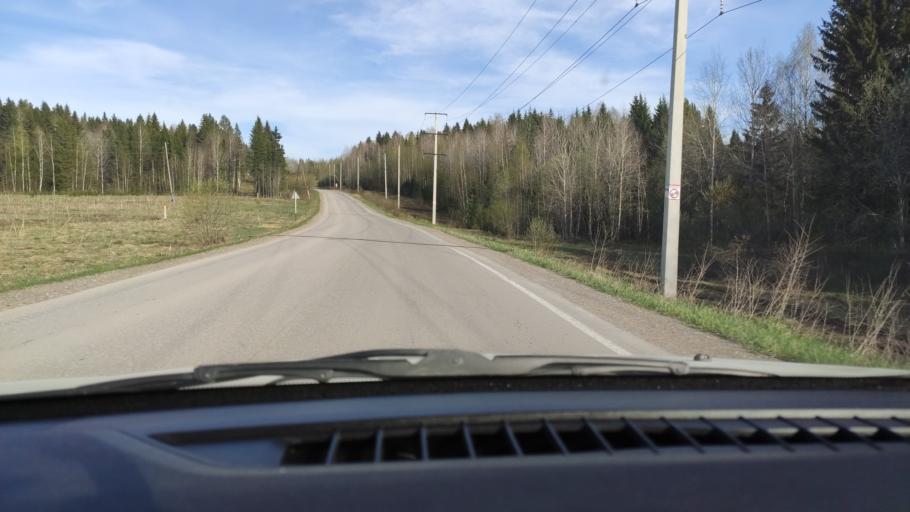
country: RU
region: Perm
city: Novyye Lyady
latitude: 57.9302
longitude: 56.6445
